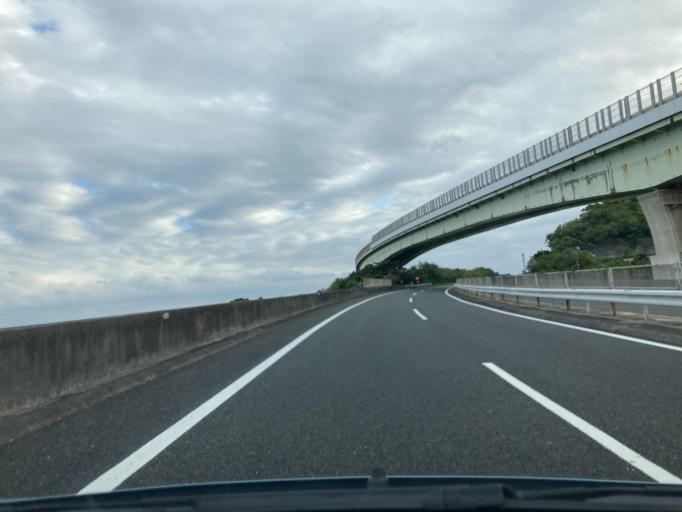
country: JP
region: Okinawa
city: Ginowan
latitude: 26.2189
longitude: 127.7395
